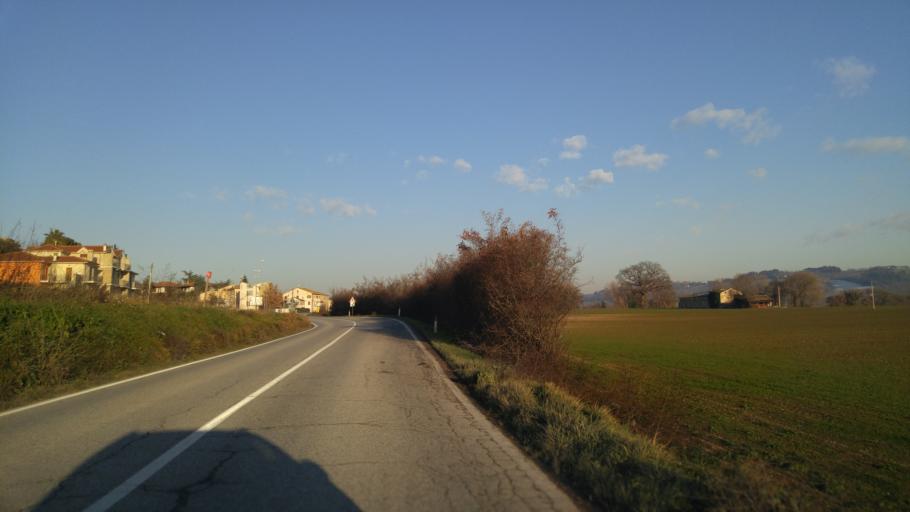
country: IT
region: The Marches
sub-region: Provincia di Pesaro e Urbino
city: Monte Porzio
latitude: 43.6858
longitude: 13.0411
